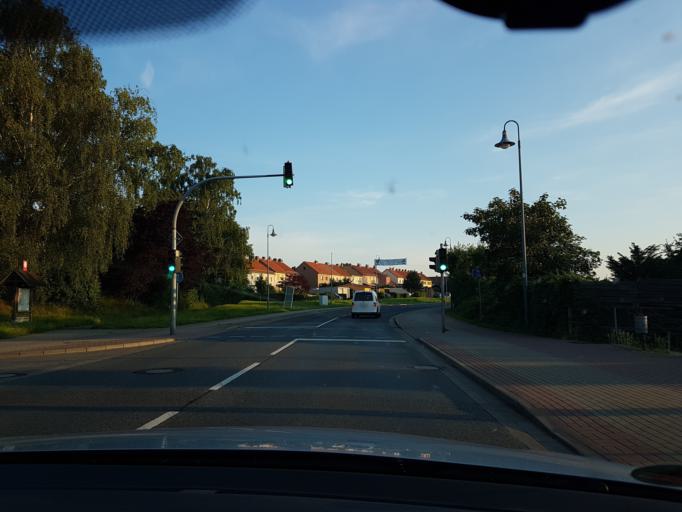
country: DE
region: Lower Saxony
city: Schoningen
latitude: 52.1455
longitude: 10.9671
